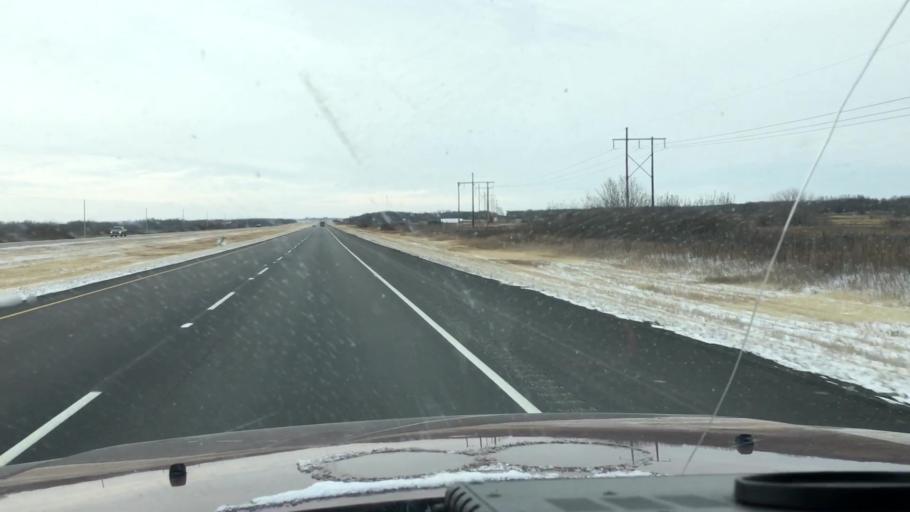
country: CA
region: Saskatchewan
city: Saskatoon
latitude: 51.8895
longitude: -106.5165
